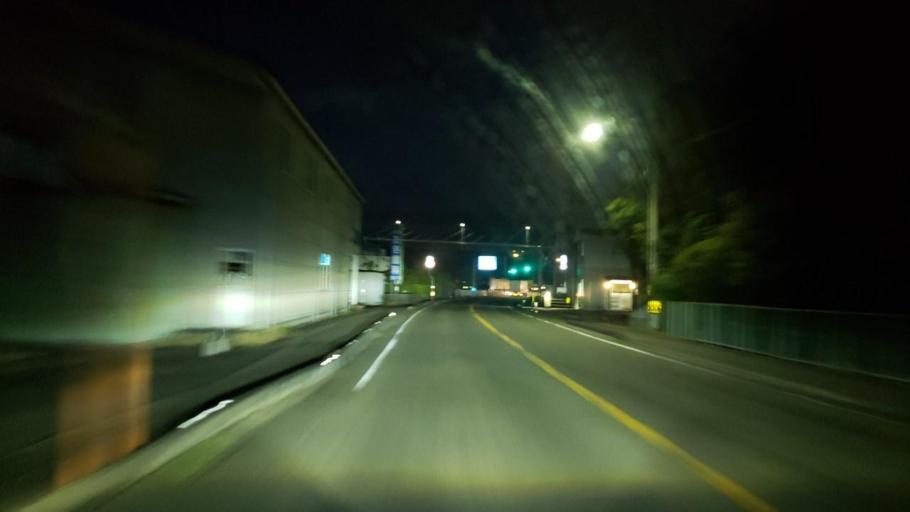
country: JP
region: Tokushima
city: Narutocho-mitsuishi
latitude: 34.2009
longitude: 134.5861
